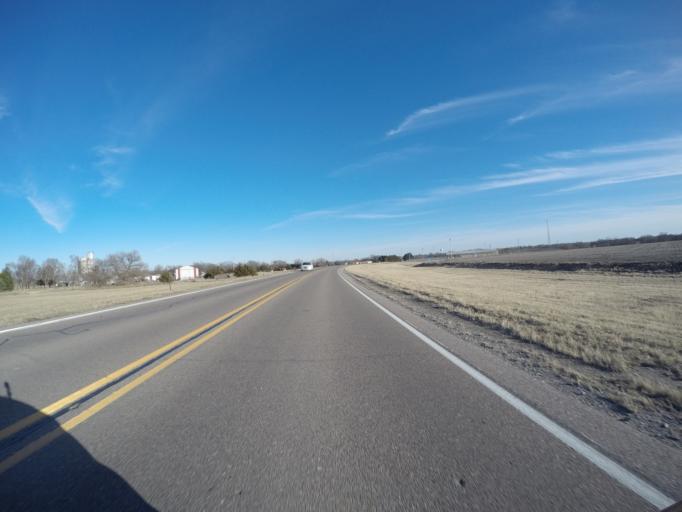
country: US
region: Nebraska
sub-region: Gage County
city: Wymore
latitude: 40.1387
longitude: -96.6771
